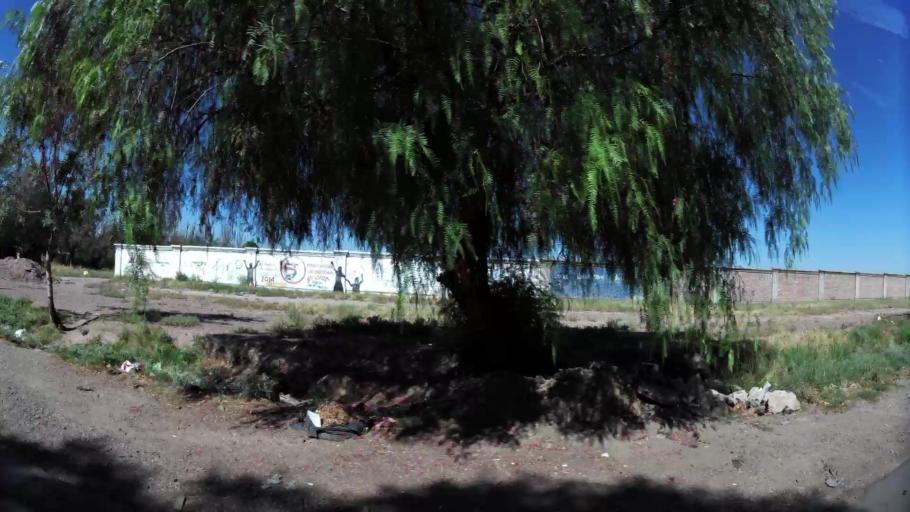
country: AR
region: Mendoza
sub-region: Departamento de Godoy Cruz
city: Godoy Cruz
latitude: -32.9542
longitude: -68.8273
